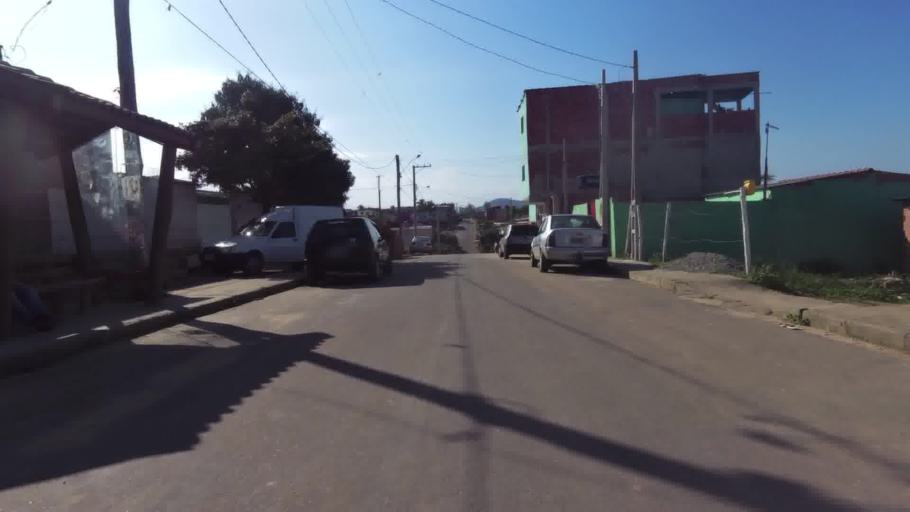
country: BR
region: Espirito Santo
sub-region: Piuma
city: Piuma
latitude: -20.8207
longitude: -40.6213
